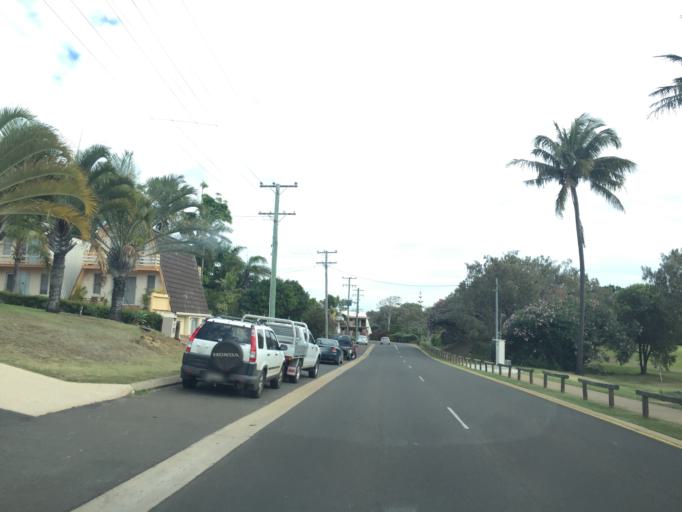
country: AU
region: Queensland
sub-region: Bundaberg
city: Bundaberg
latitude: -24.8200
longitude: 152.4651
